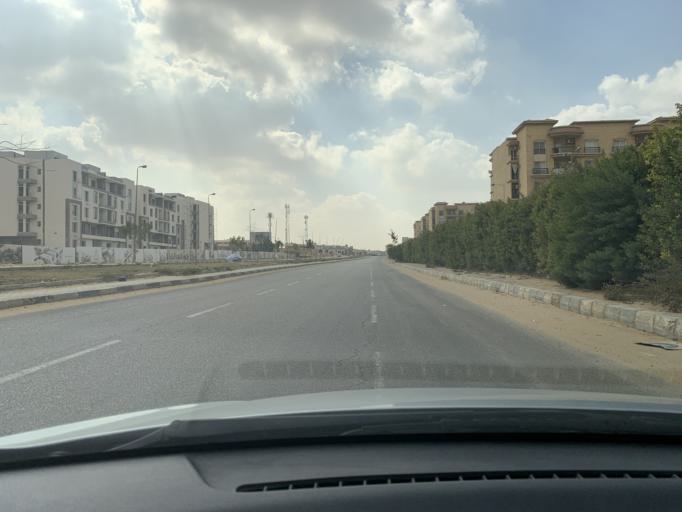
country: EG
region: Muhafazat al Qalyubiyah
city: Al Khankah
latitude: 30.0653
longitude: 31.5191
